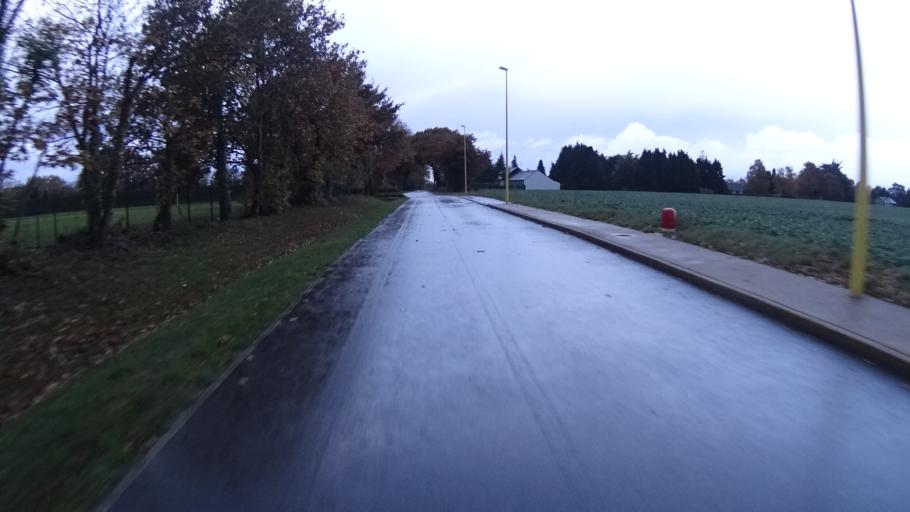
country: FR
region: Brittany
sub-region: Departement d'Ille-et-Vilaine
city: Bains-sur-Oust
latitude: 47.6853
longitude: -2.0498
